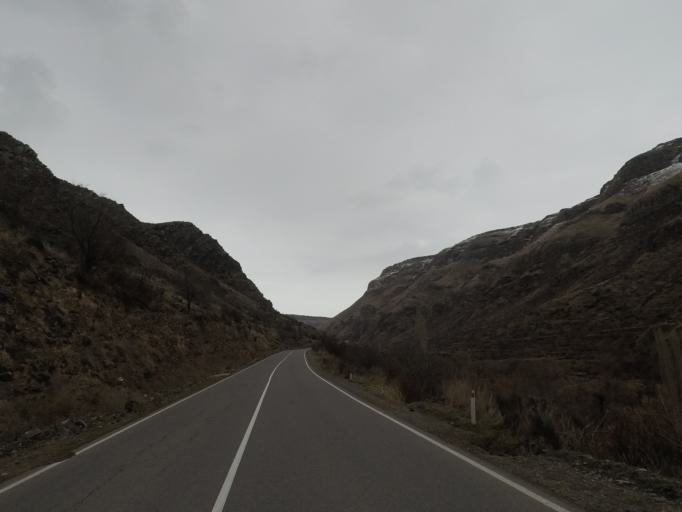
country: GE
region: Samtskhe-Javakheti
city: Aspindza
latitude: 41.4815
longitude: 43.2890
